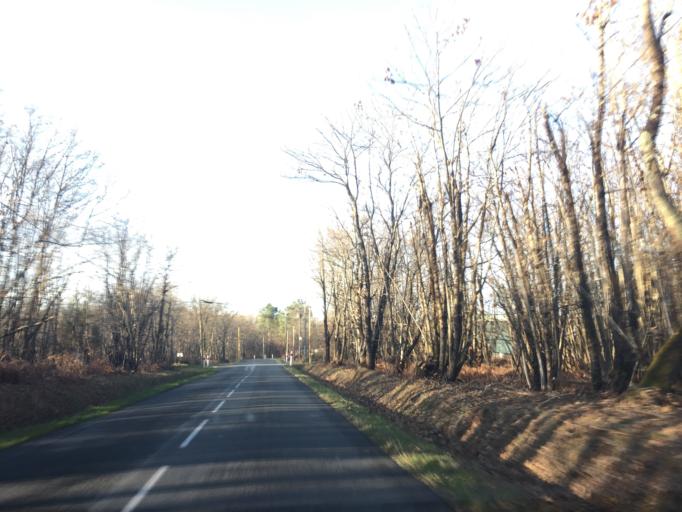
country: FR
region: Aquitaine
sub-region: Departement de la Dordogne
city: Riberac
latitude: 45.2082
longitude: 0.3091
